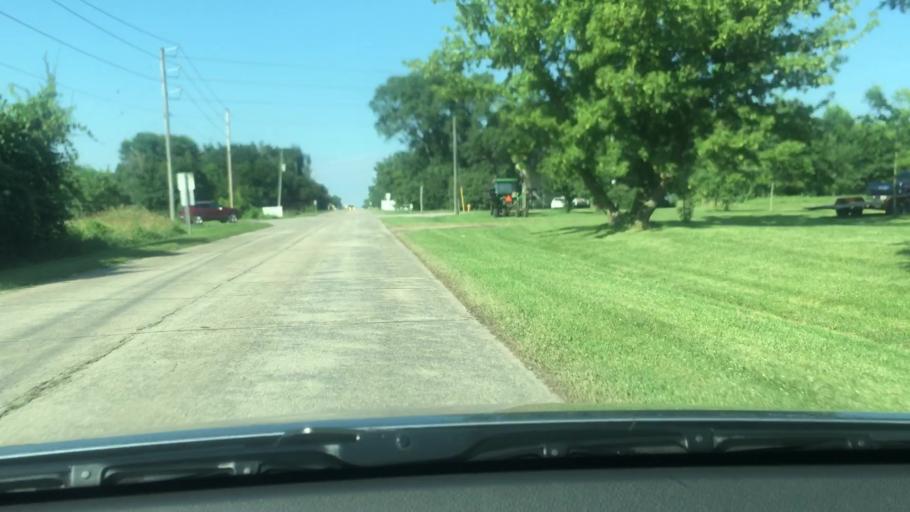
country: US
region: Wisconsin
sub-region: Winnebago County
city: Oshkosh
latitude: 43.9660
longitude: -88.5683
